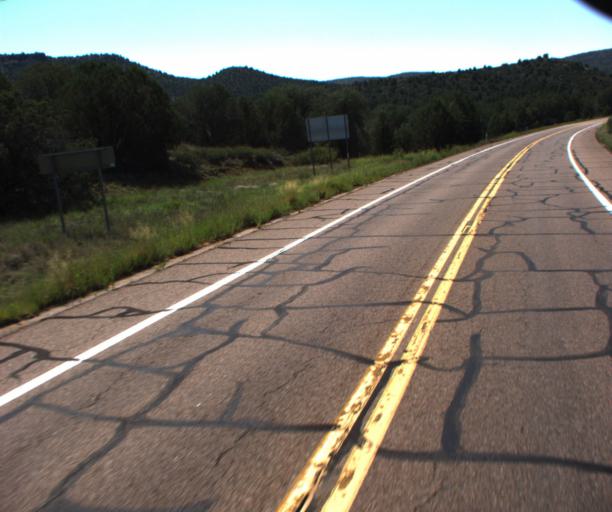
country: US
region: Arizona
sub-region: Navajo County
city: Cibecue
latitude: 33.7659
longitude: -110.5108
